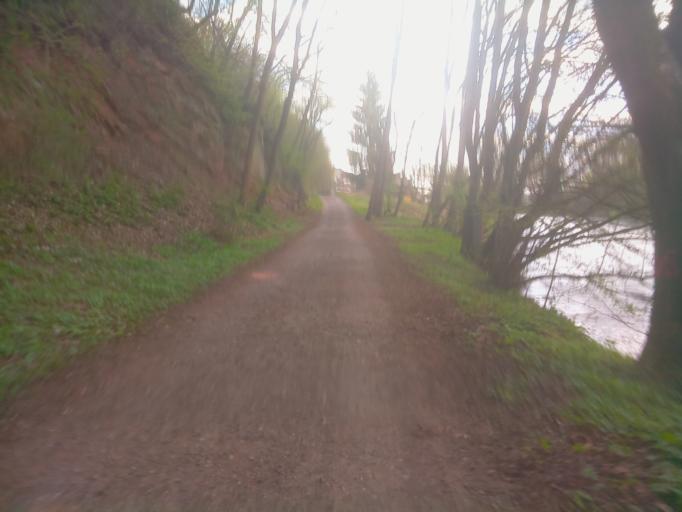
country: DE
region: Thuringia
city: Kahla
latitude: 50.8047
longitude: 11.5959
